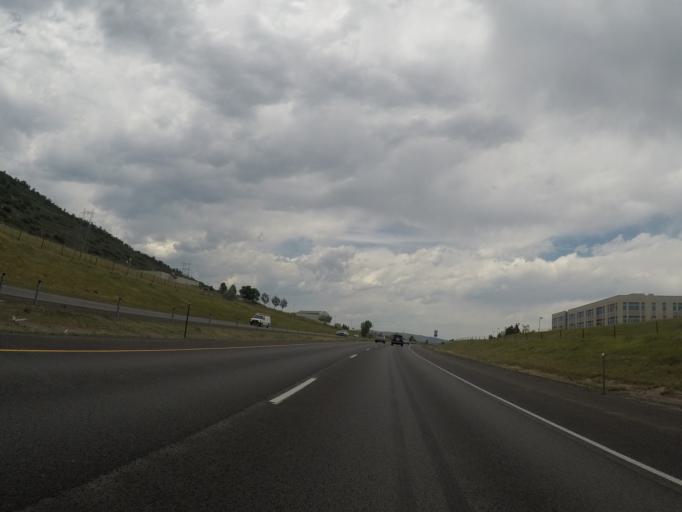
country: US
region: Colorado
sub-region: Jefferson County
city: Ken Caryl
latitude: 39.6029
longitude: -105.1536
